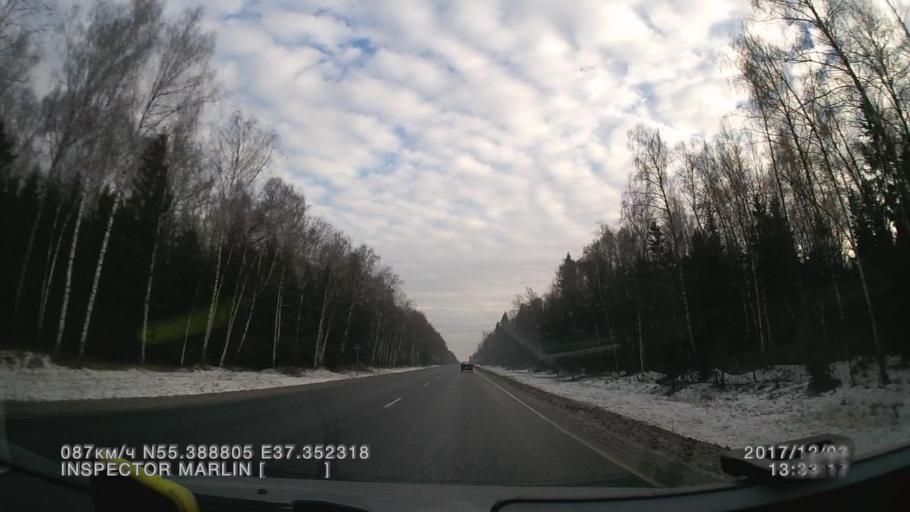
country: RU
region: Moskovskaya
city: Troitsk
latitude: 55.3887
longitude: 37.3526
